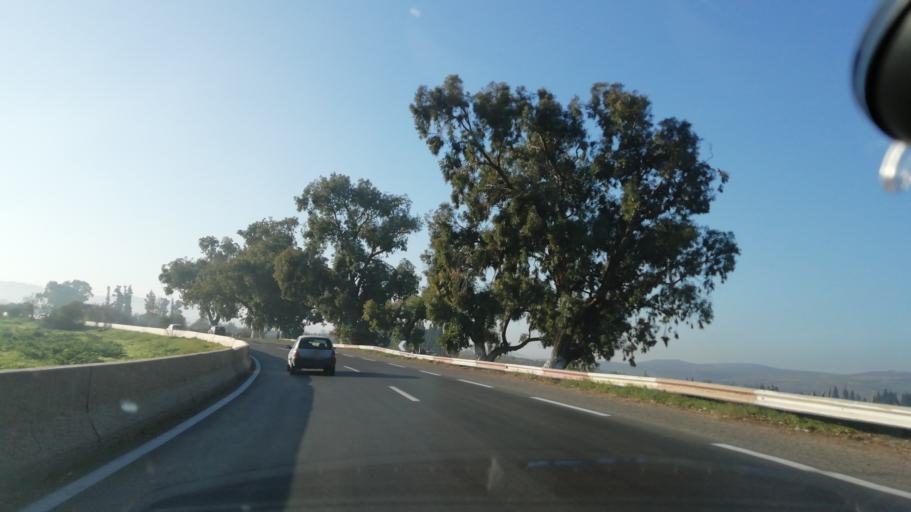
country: DZ
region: Tlemcen
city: Remchi
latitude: 35.1053
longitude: -1.4424
